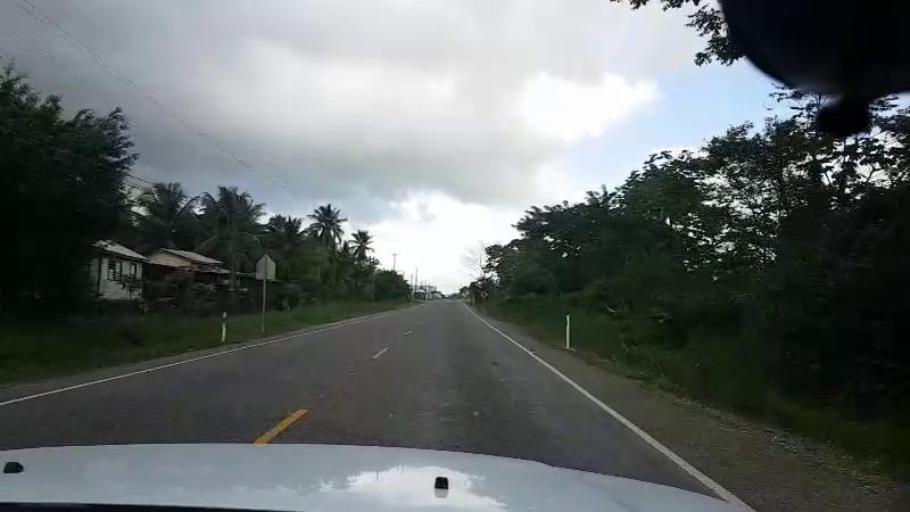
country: BZ
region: Stann Creek
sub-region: Dangriga
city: Dangriga
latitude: 16.9929
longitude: -88.3750
